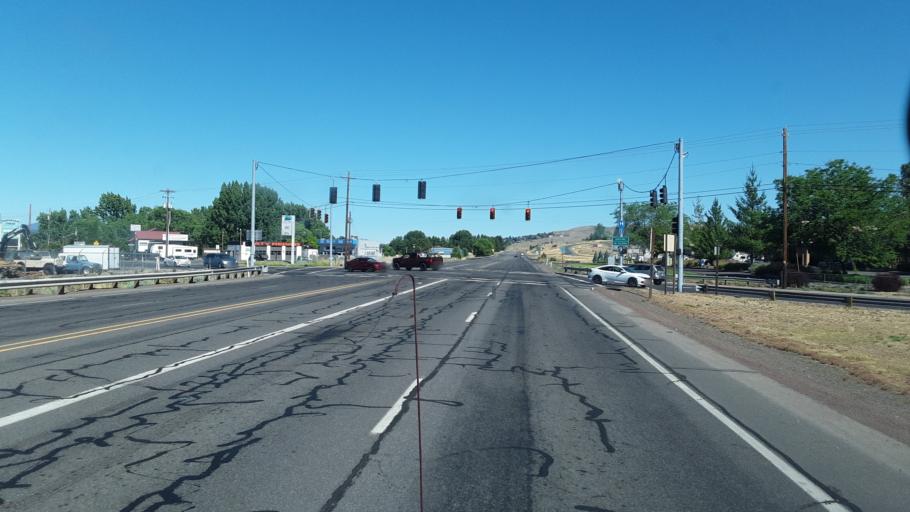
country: US
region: Oregon
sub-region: Klamath County
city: Altamont
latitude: 42.2134
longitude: -121.7429
